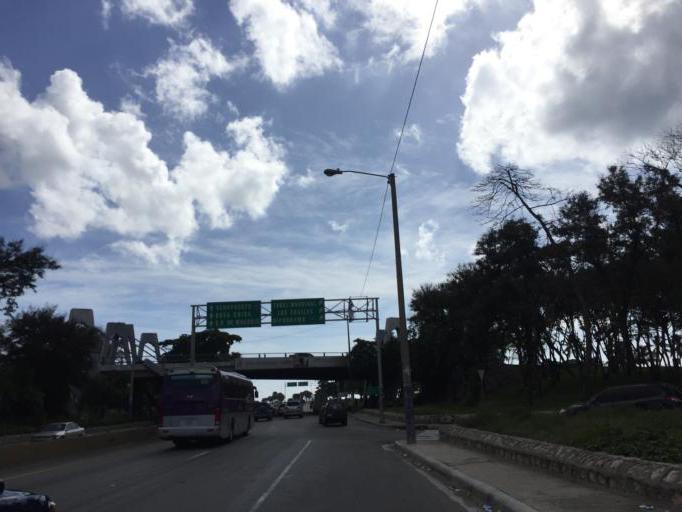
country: DO
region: Santo Domingo
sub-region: Santo Domingo
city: Santo Domingo Este
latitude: 18.4705
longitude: -69.8309
